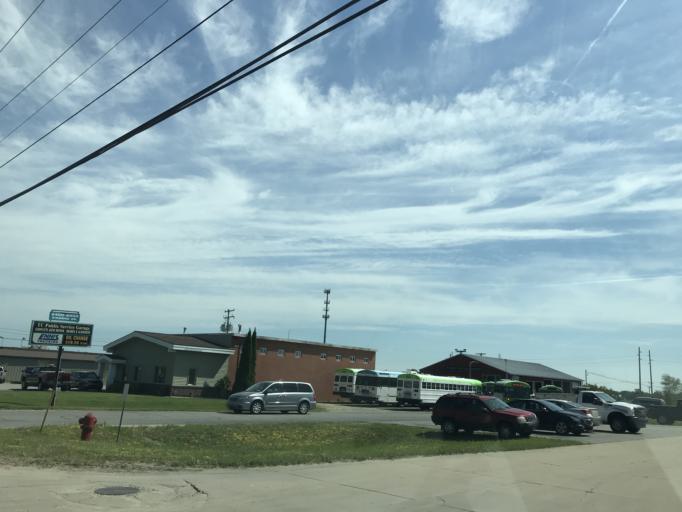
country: US
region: Michigan
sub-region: Grand Traverse County
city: Traverse City
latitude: 44.7293
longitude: -85.6258
